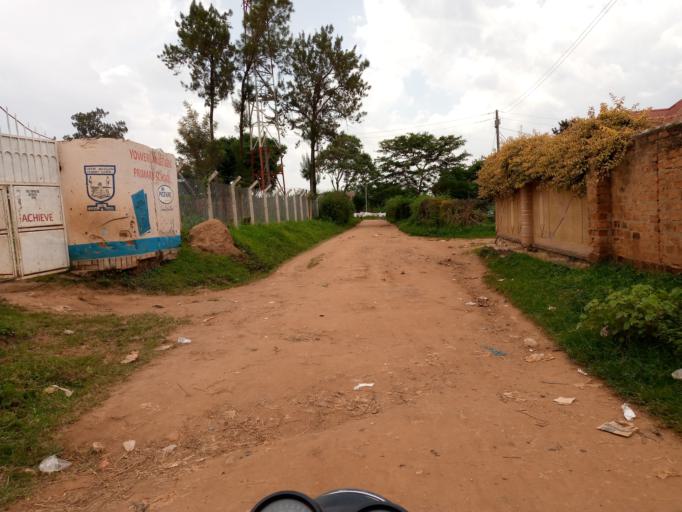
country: UG
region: Eastern Region
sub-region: Mbale District
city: Mbale
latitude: 1.0825
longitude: 34.1696
